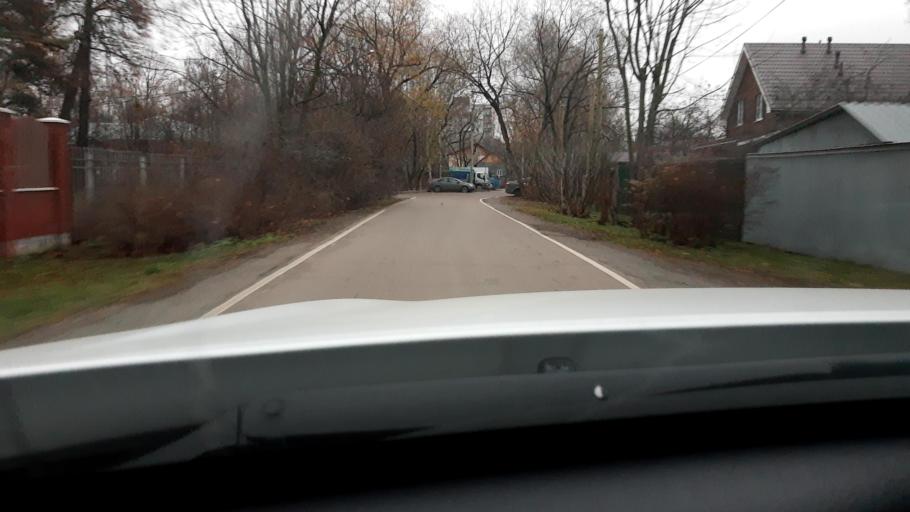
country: RU
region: Moscow
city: Zhulebino
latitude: 55.7152
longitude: 37.8526
